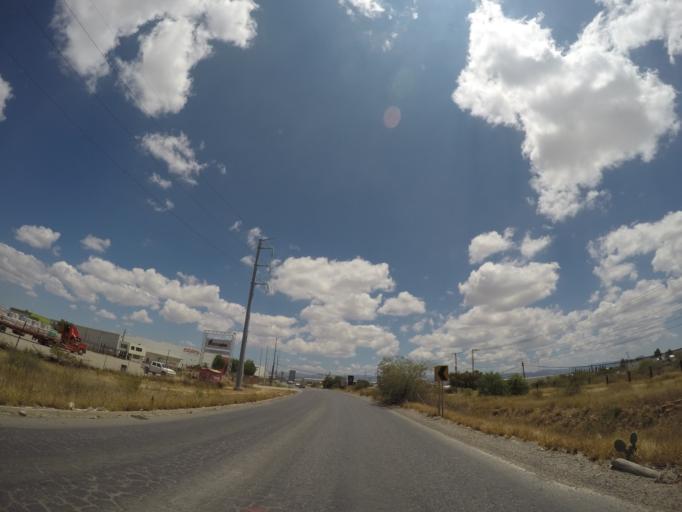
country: MX
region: San Luis Potosi
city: La Pila
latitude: 22.0411
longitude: -100.8872
